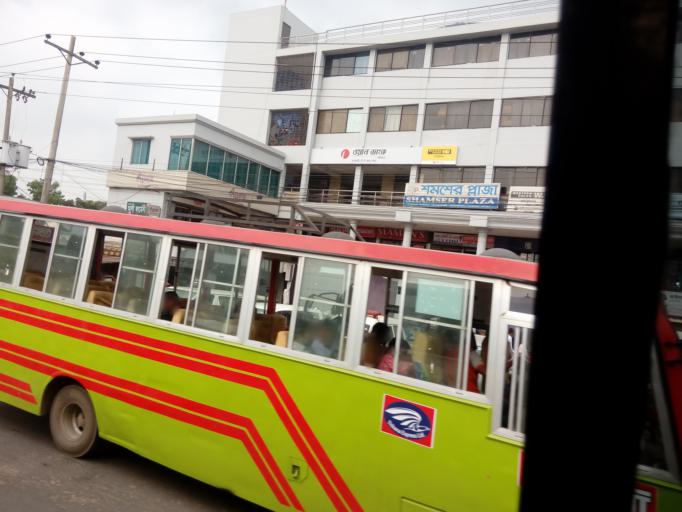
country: BD
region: Dhaka
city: Tungi
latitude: 23.9536
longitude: 90.2732
